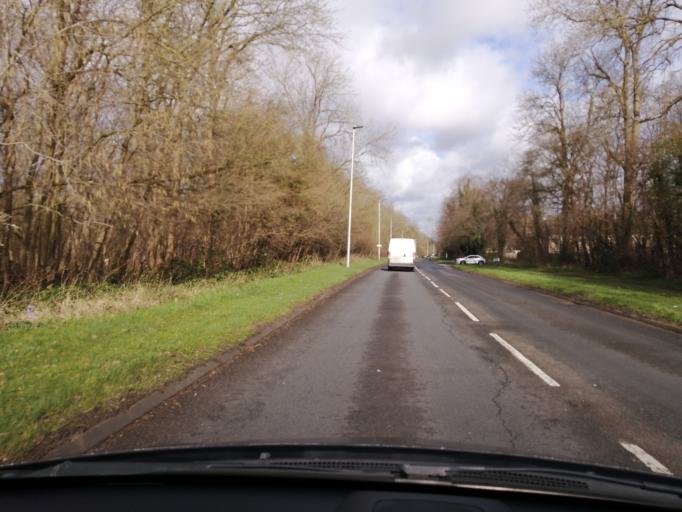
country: GB
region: England
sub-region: Peterborough
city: Marholm
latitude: 52.5938
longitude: -0.2877
